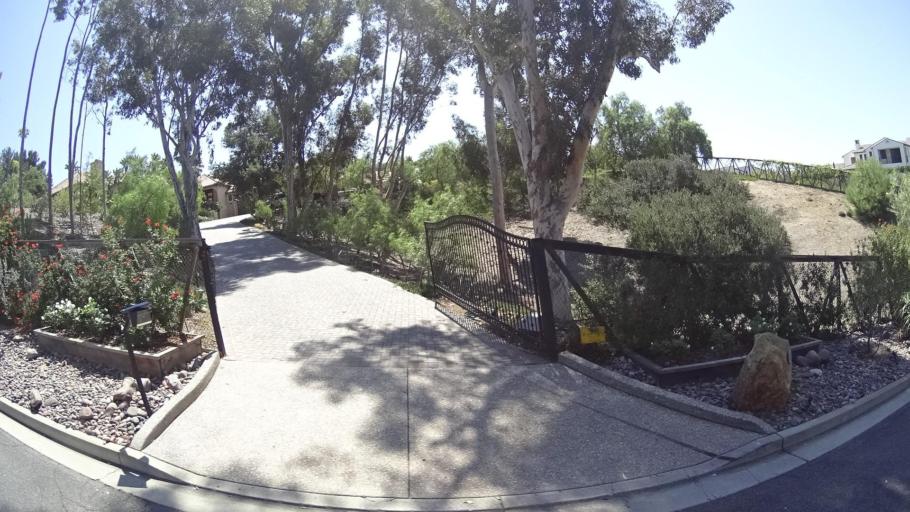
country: US
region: California
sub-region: San Diego County
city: Fairbanks Ranch
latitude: 32.9738
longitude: -117.1781
